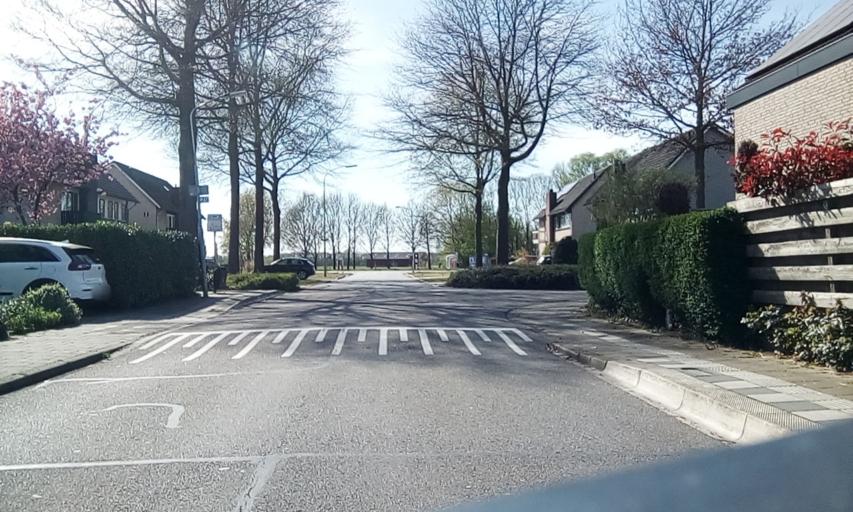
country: NL
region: Gelderland
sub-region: Gemeente Wijchen
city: Wijchen
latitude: 51.8105
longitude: 5.7046
